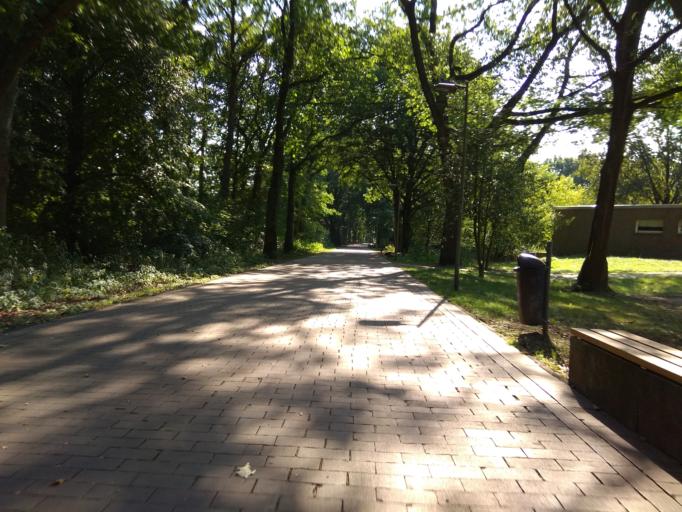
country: DE
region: North Rhine-Westphalia
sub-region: Regierungsbezirk Munster
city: Klein Reken
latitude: 51.7307
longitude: 7.0373
